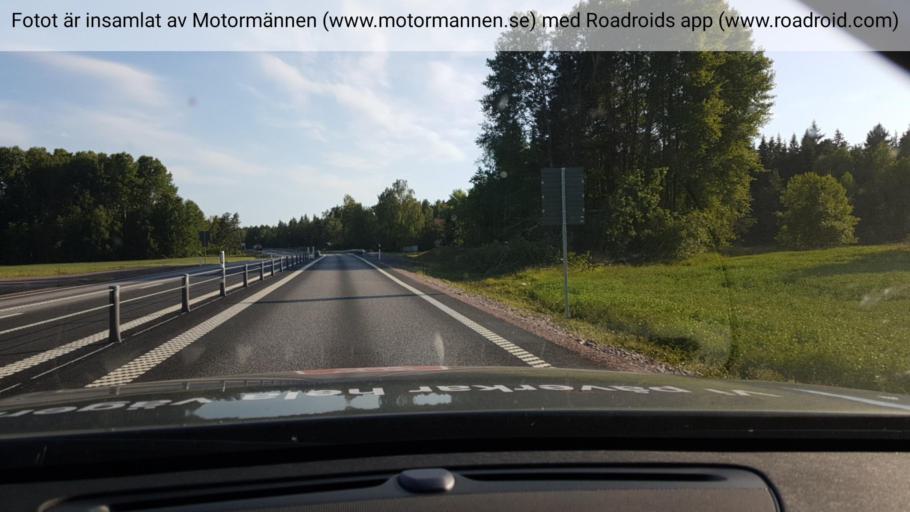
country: SE
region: Uppsala
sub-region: Osthammars Kommun
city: Gimo
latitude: 60.1153
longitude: 18.1340
